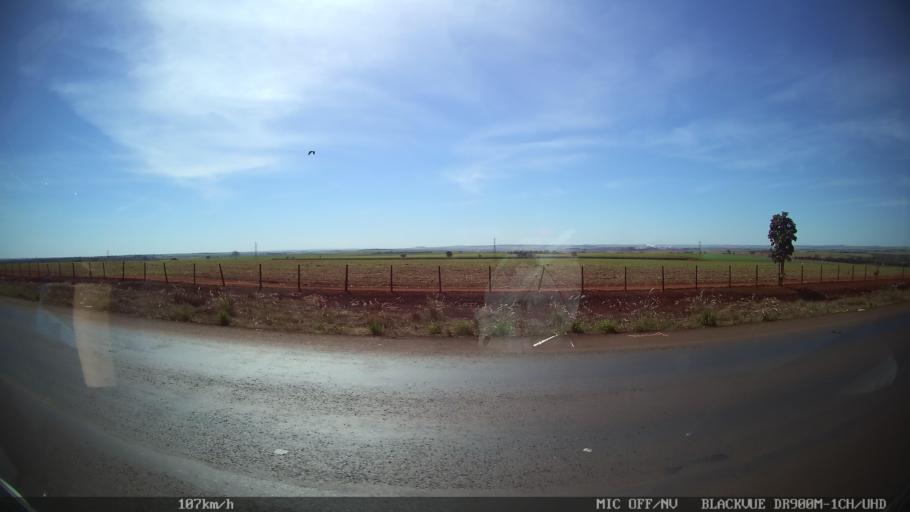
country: BR
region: Sao Paulo
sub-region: Sao Joaquim Da Barra
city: Sao Joaquim da Barra
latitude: -20.5122
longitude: -47.9014
